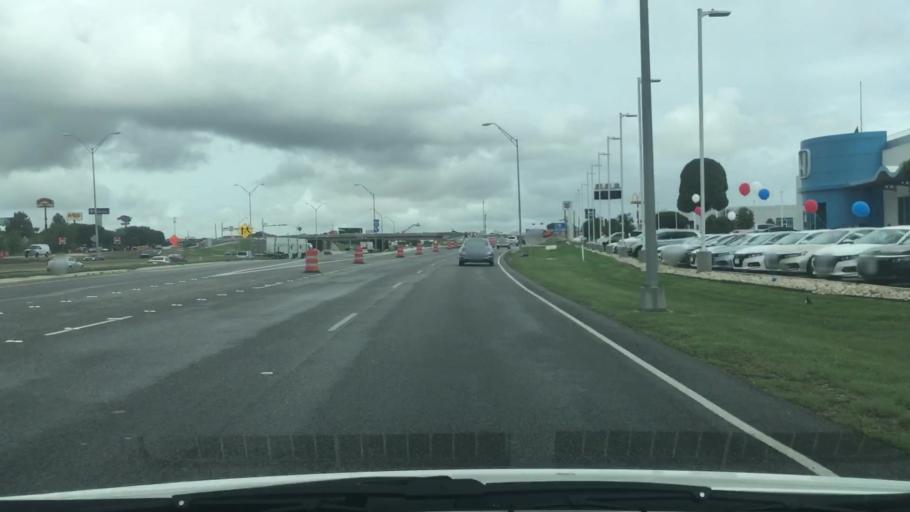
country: US
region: Texas
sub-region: Williamson County
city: Round Rock
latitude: 30.5317
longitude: -97.6910
